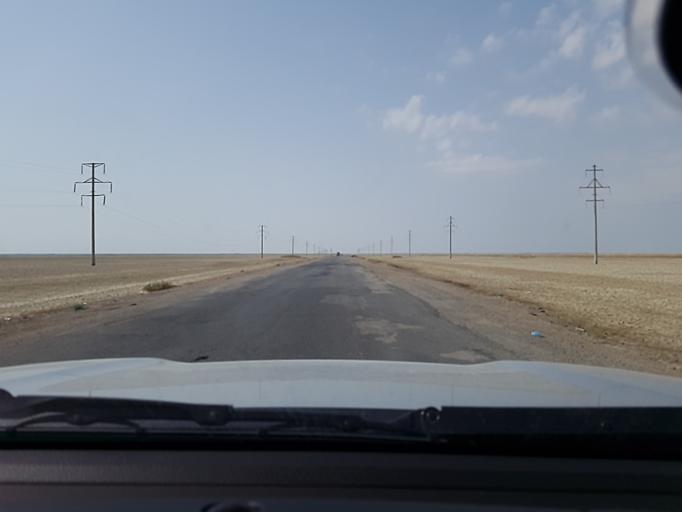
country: TM
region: Balkan
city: Gumdag
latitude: 39.0694
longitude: 54.5843
